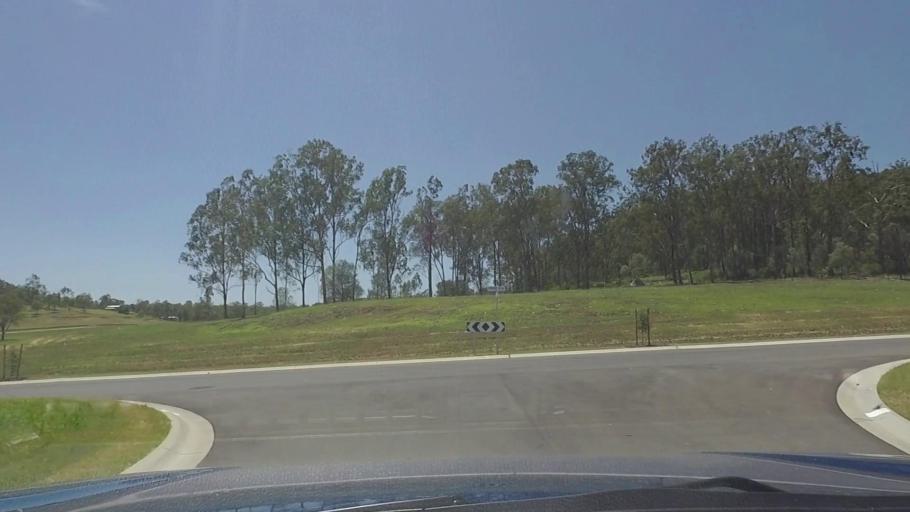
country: AU
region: Queensland
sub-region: Logan
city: Cedar Vale
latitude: -27.8903
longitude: 152.9864
